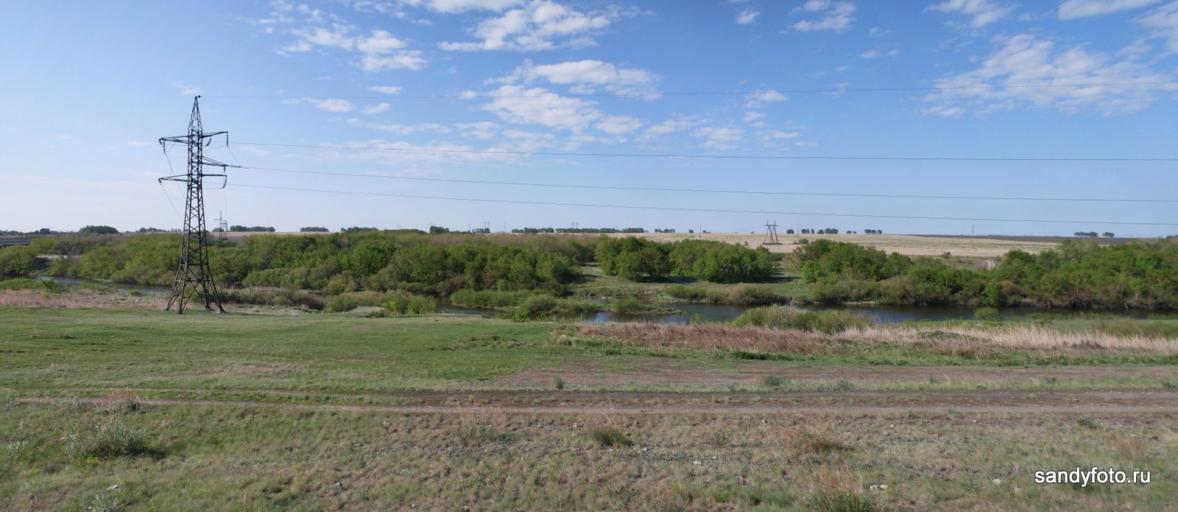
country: RU
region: Chelyabinsk
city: Troitsk
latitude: 54.1246
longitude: 61.4766
